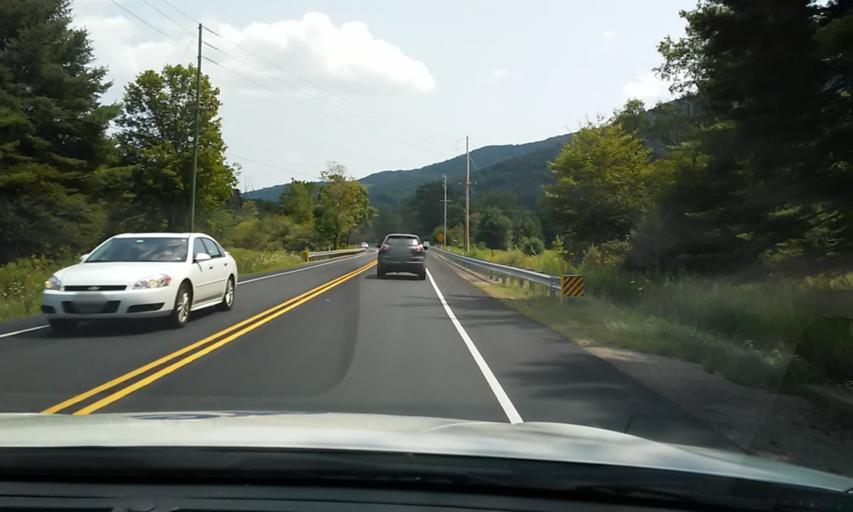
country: US
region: Pennsylvania
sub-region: Cameron County
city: Emporium
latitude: 41.4754
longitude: -78.3616
